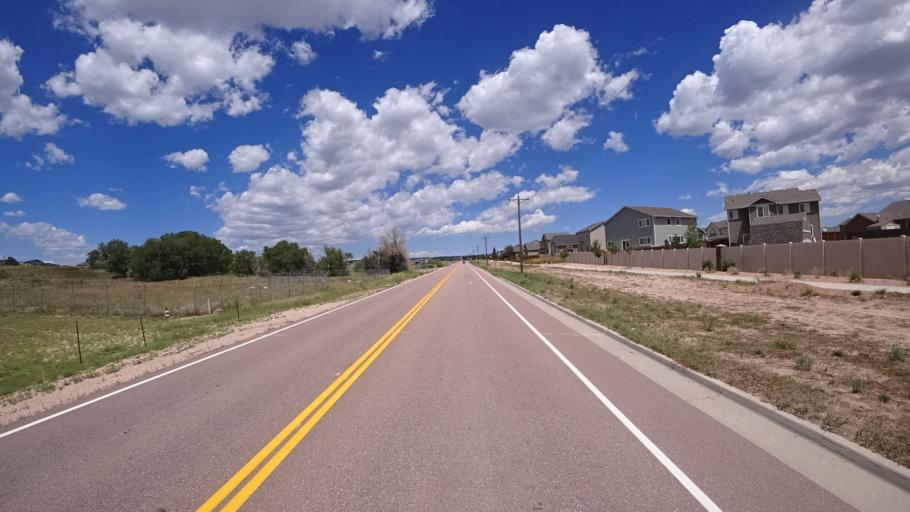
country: US
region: Colorado
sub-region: El Paso County
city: Black Forest
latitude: 38.9463
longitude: -104.7009
